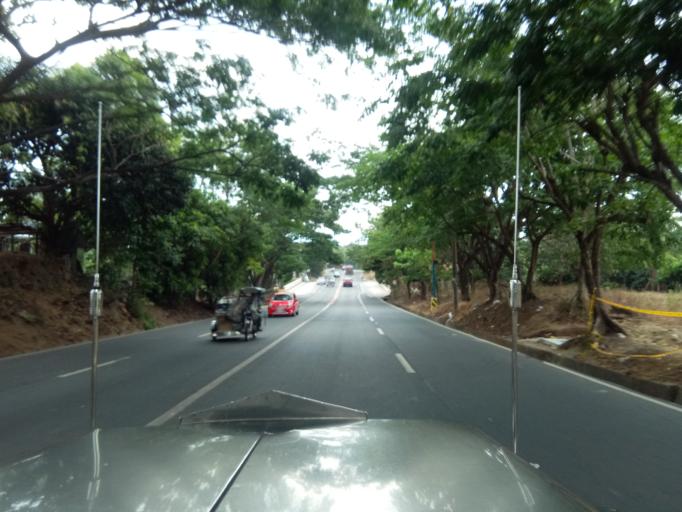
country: PH
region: Calabarzon
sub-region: Province of Cavite
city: Aliang
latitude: 14.2844
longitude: 120.8937
